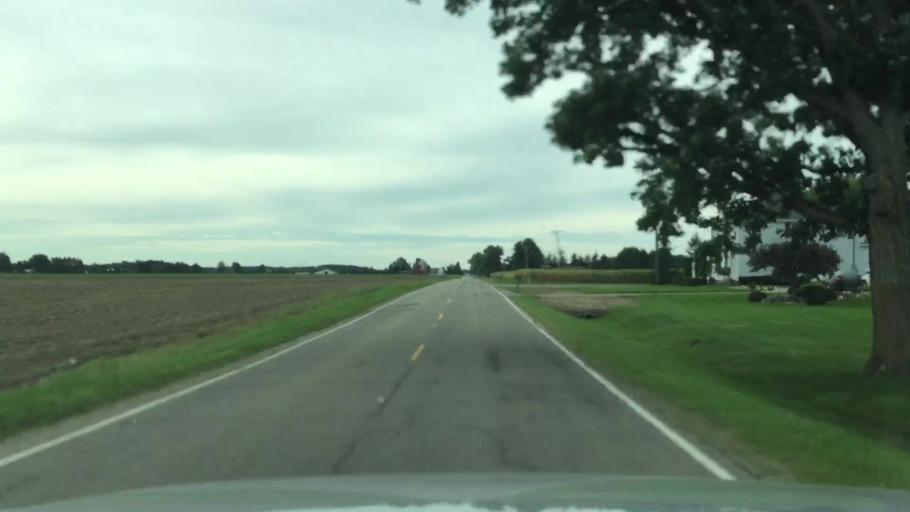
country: US
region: Michigan
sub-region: Genesee County
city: Montrose
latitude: 43.0875
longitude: -83.9878
